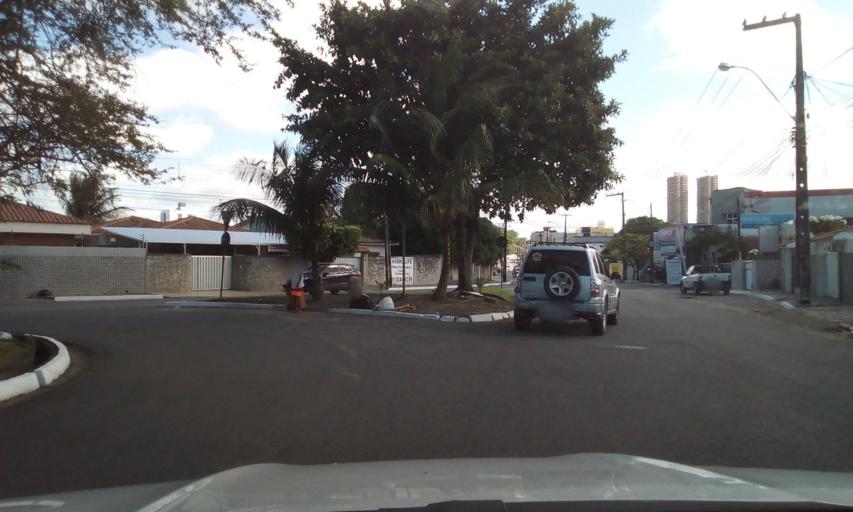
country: BR
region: Paraiba
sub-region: Joao Pessoa
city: Joao Pessoa
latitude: -7.1112
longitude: -34.8584
